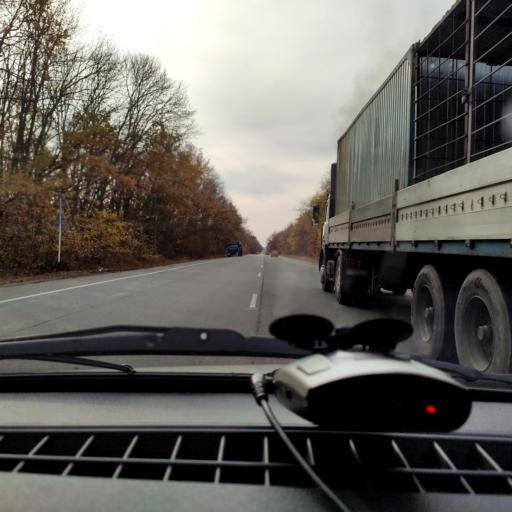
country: RU
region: Voronezj
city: Devitsa
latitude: 51.6307
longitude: 38.9919
